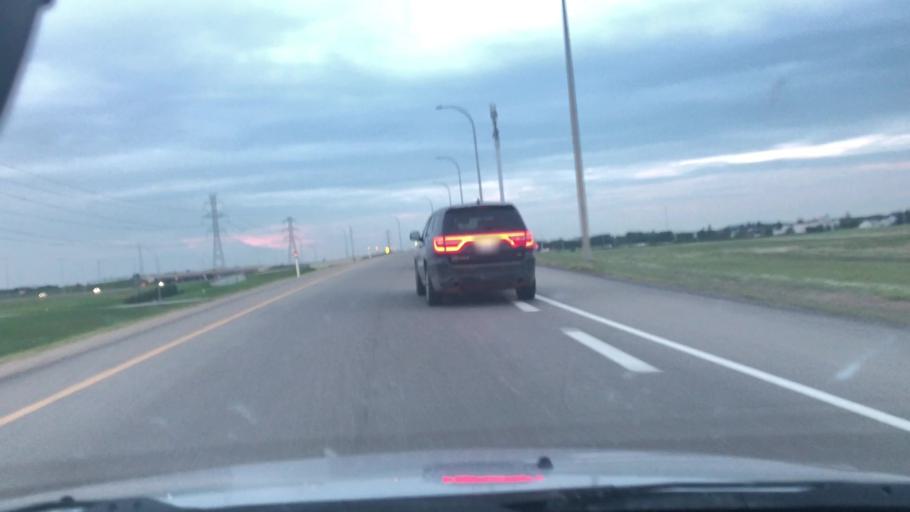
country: CA
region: Alberta
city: St. Albert
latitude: 53.5160
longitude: -113.6568
